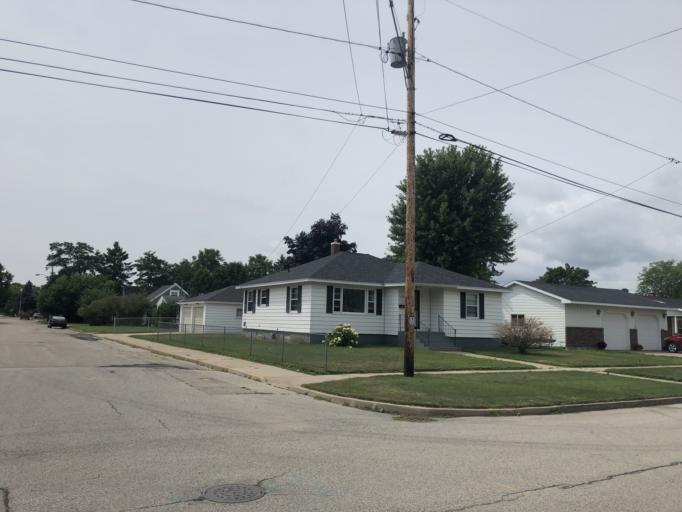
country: US
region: Michigan
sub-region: Menominee County
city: Menominee
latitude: 45.1171
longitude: -87.6236
